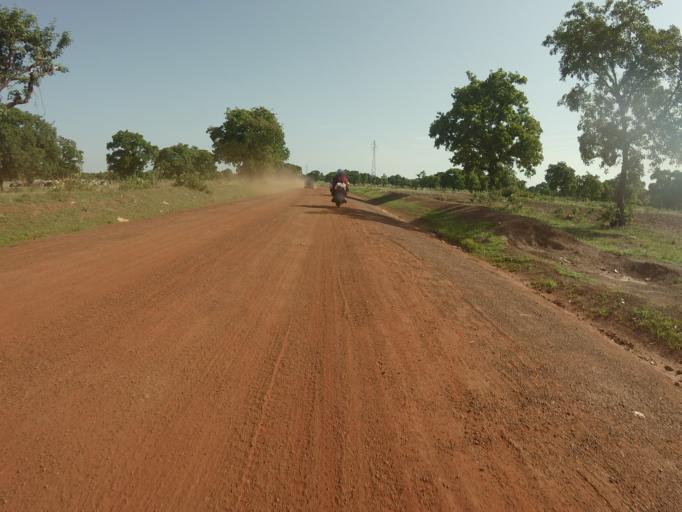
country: GH
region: Upper East
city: Bawku
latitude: 10.7791
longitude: -0.1916
